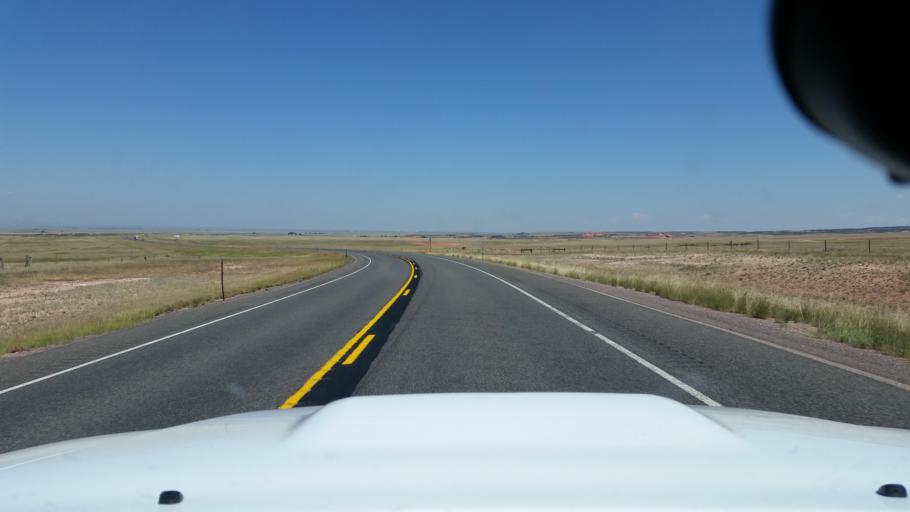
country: US
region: Wyoming
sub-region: Albany County
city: Laramie
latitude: 41.1336
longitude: -105.5517
